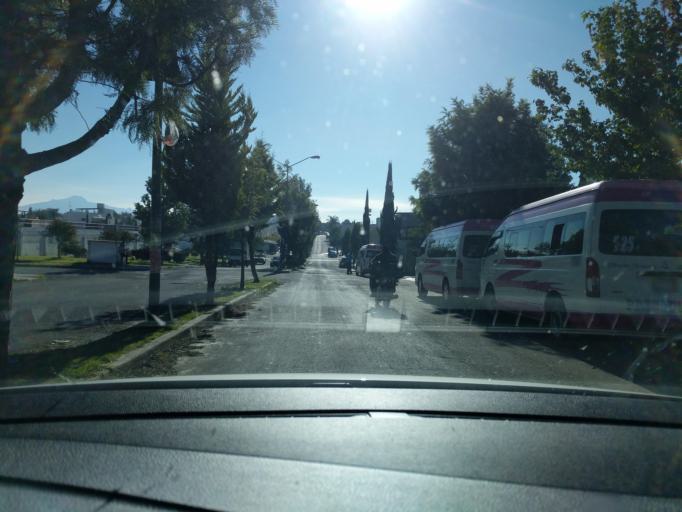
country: MX
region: Puebla
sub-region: Huejotzingo
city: Los Encinos
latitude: 19.1776
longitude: -98.3937
